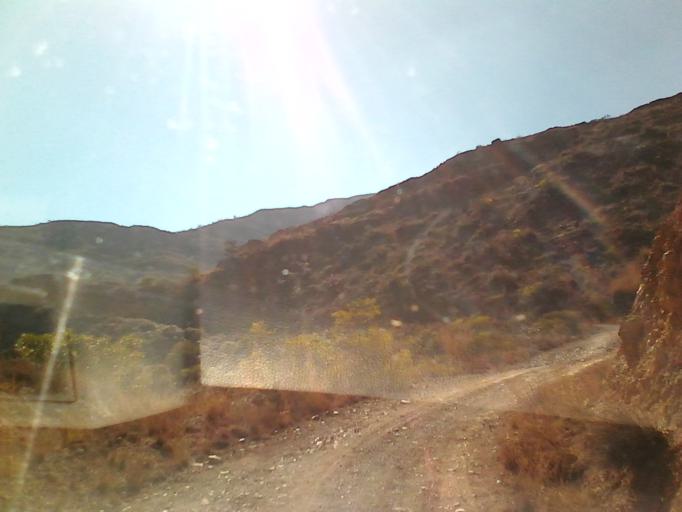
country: CO
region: Boyaca
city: Sachica
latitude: 5.5548
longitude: -73.5475
